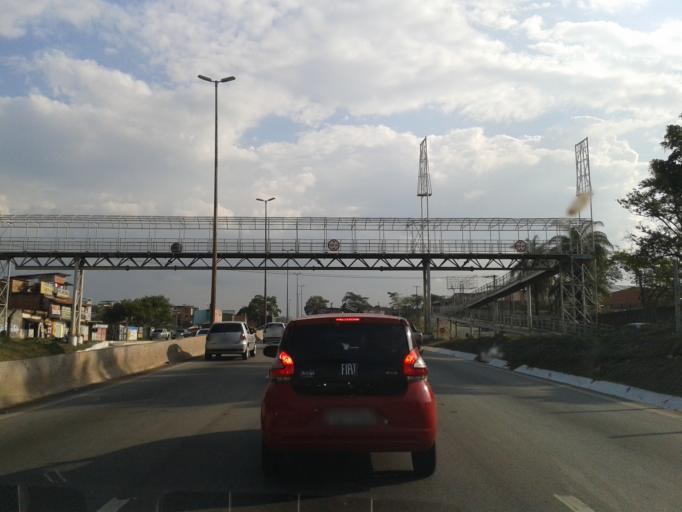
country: BR
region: Minas Gerais
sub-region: Belo Horizonte
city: Belo Horizonte
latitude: -19.8713
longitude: -43.9480
